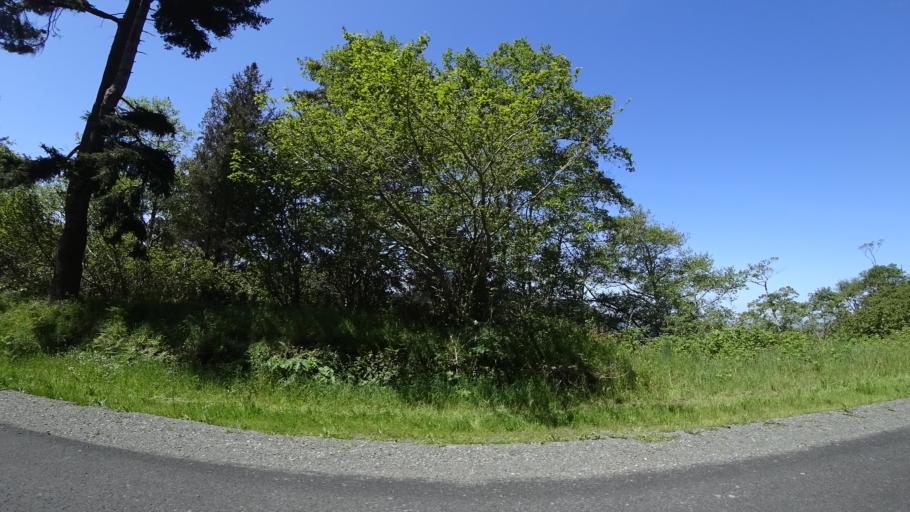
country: US
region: California
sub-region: Humboldt County
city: Westhaven-Moonstone
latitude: 41.2408
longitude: -124.0846
